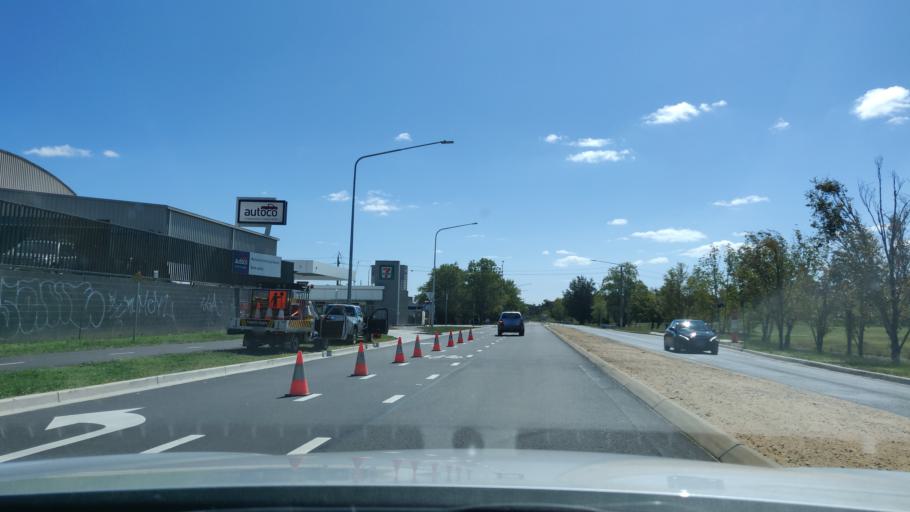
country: AU
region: Australian Capital Territory
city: Forrest
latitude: -35.3559
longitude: 149.0915
